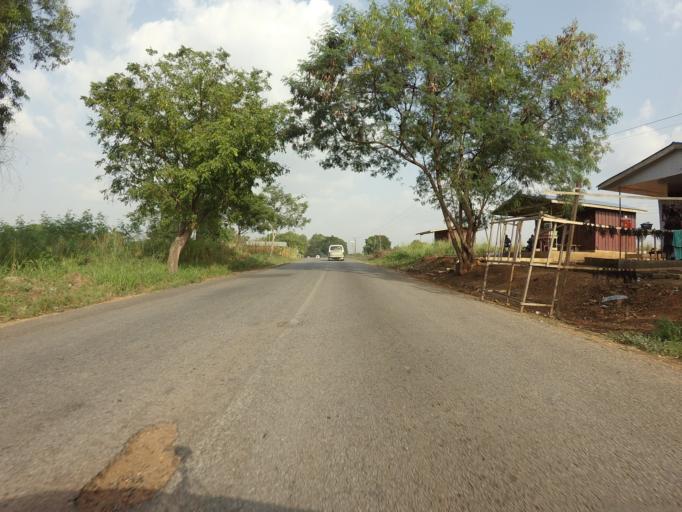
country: GH
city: Akropong
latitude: 6.2432
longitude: 0.1228
